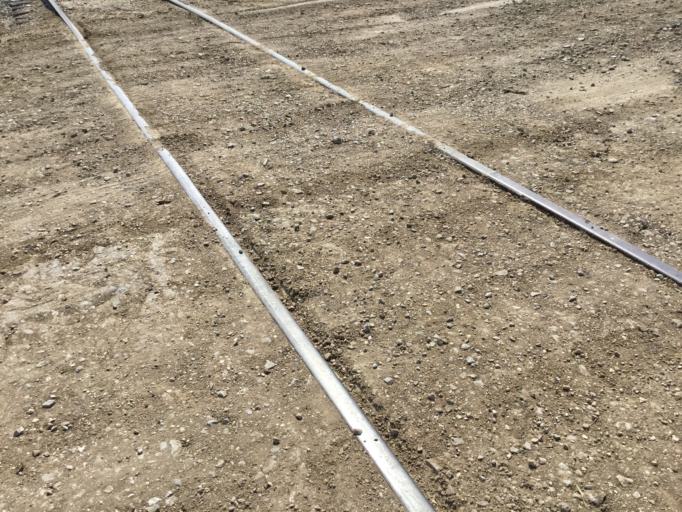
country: US
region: Kansas
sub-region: Mitchell County
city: Beloit
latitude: 39.5218
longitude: -98.3904
